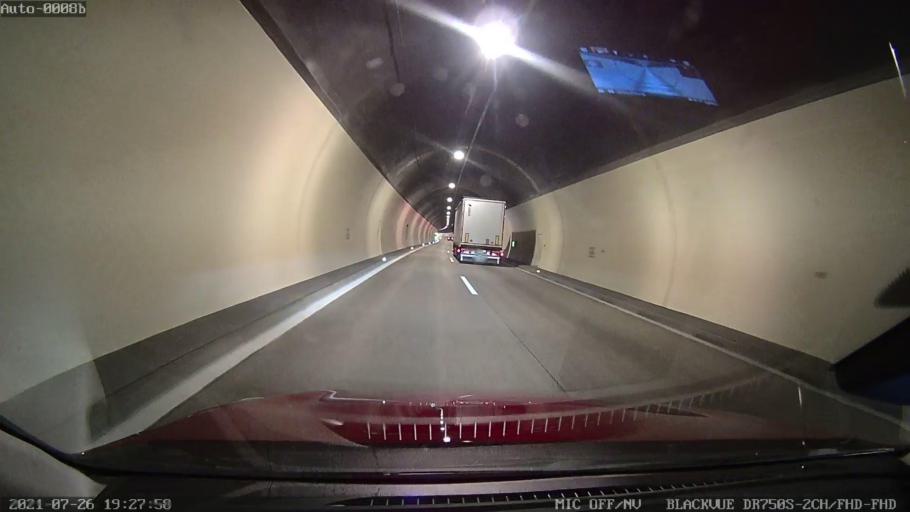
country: AT
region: Upper Austria
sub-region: Politischer Bezirk Kirchdorf an der Krems
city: Micheldorf in Oberoesterreich
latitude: 47.8160
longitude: 14.1698
